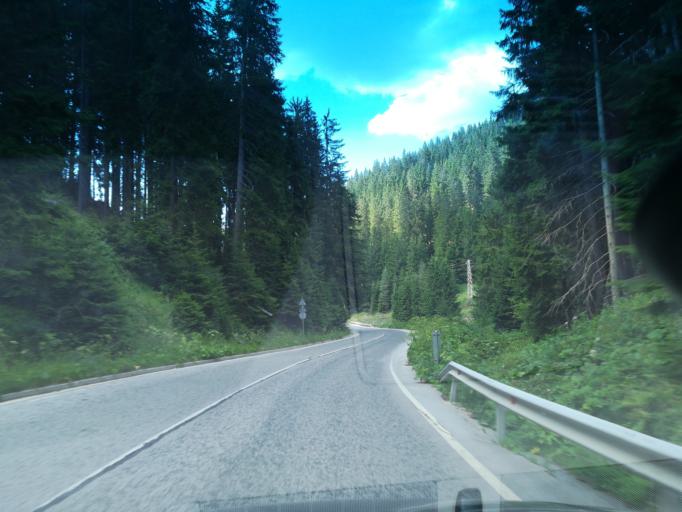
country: BG
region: Smolyan
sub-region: Obshtina Chepelare
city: Chepelare
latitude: 41.6686
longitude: 24.7145
